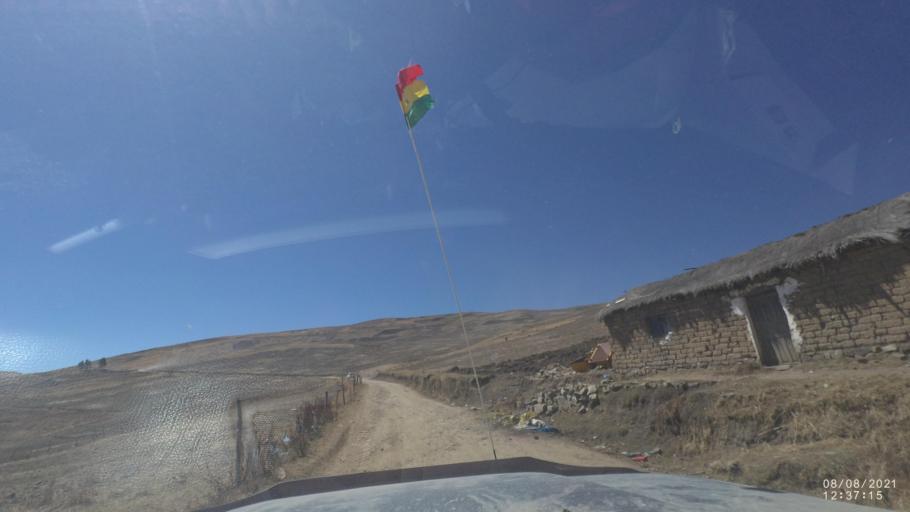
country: BO
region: Cochabamba
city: Colchani
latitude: -16.8383
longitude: -66.6279
